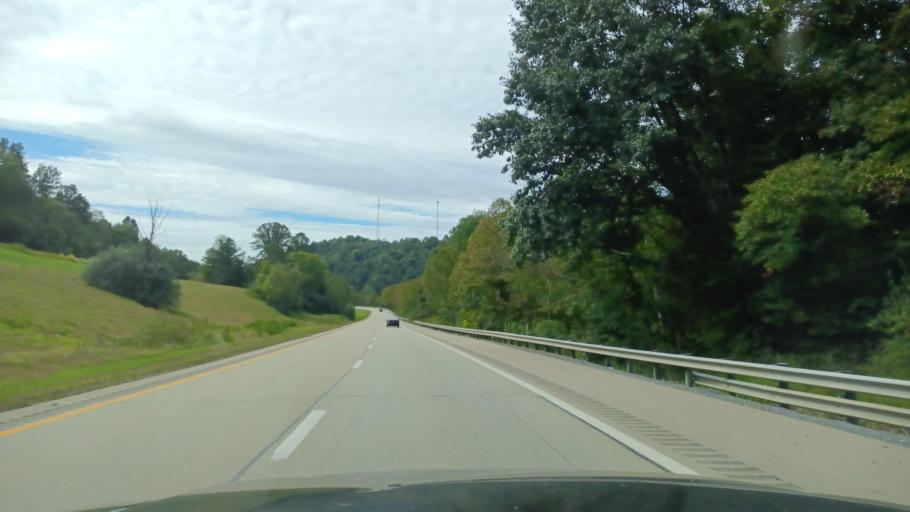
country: US
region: West Virginia
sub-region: Doddridge County
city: West Union
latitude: 39.2988
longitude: -80.7514
